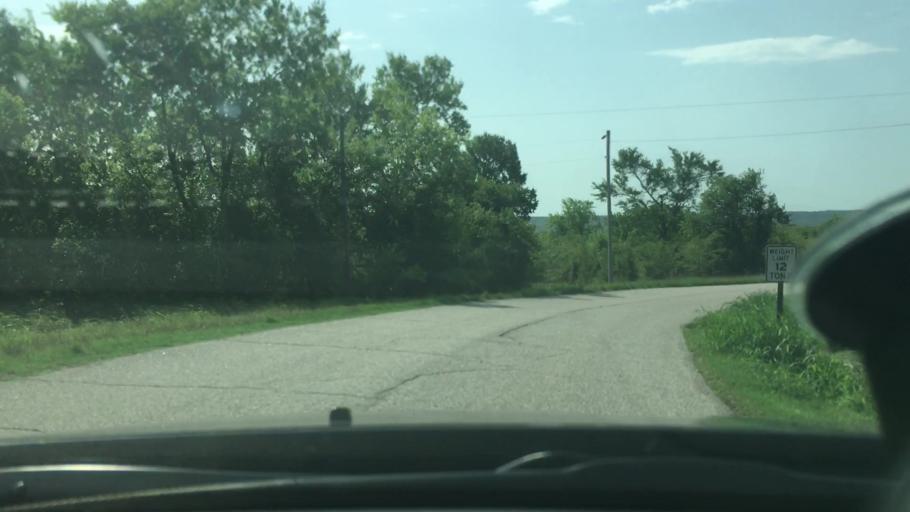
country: US
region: Oklahoma
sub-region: Atoka County
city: Atoka
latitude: 34.4682
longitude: -96.0409
